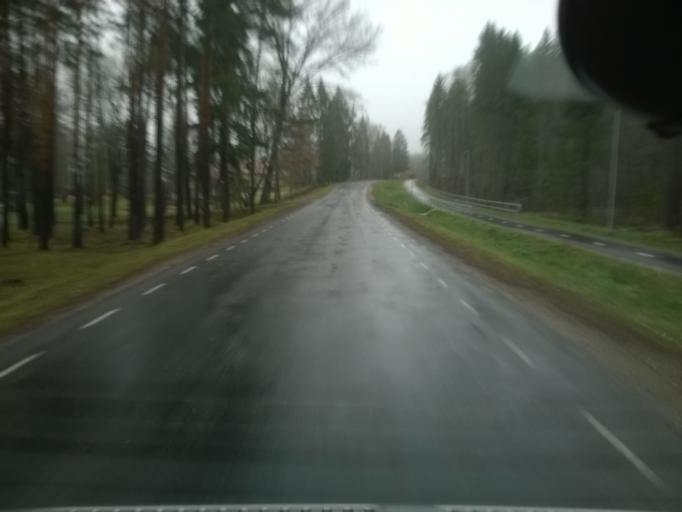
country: EE
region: Raplamaa
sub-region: Kohila vald
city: Kohila
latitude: 59.1705
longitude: 24.6533
